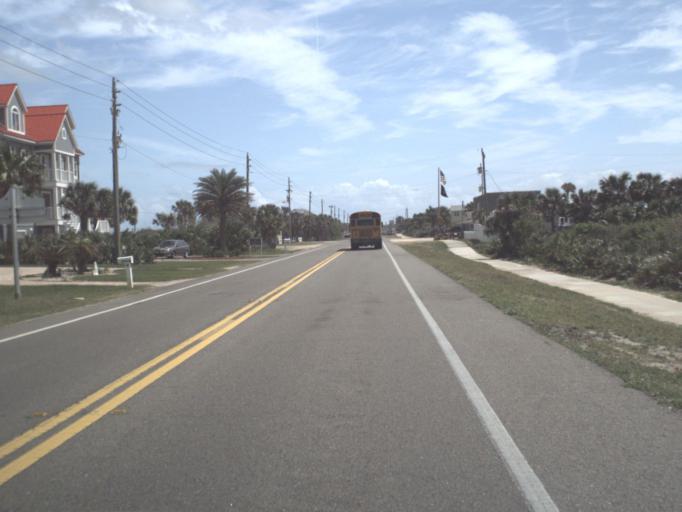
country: US
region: Florida
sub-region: Flagler County
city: Flagler Beach
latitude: 29.5286
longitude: -81.1514
